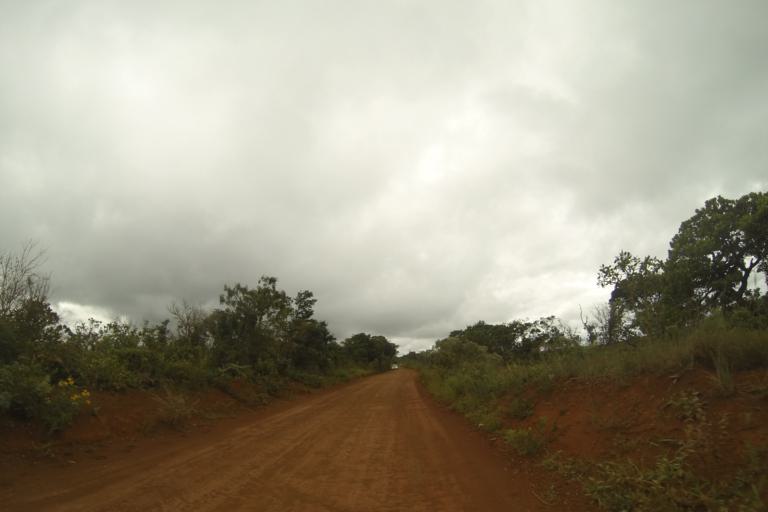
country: BR
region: Minas Gerais
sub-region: Campos Altos
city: Campos Altos
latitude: -19.8261
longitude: -46.3229
